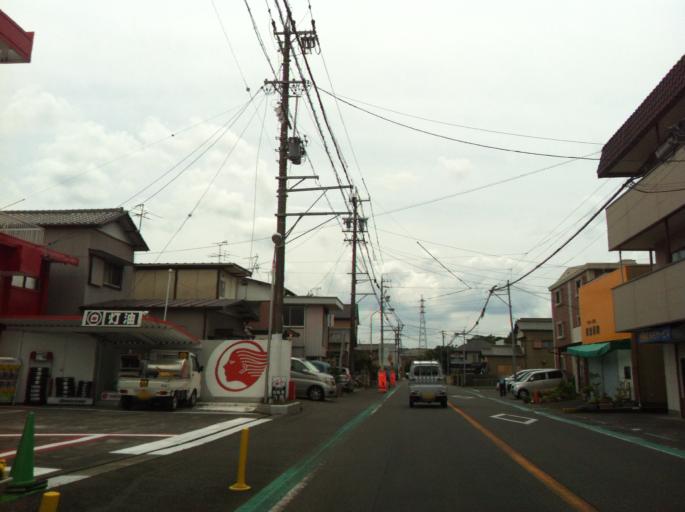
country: JP
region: Shizuoka
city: Shizuoka-shi
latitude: 35.0553
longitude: 138.4245
